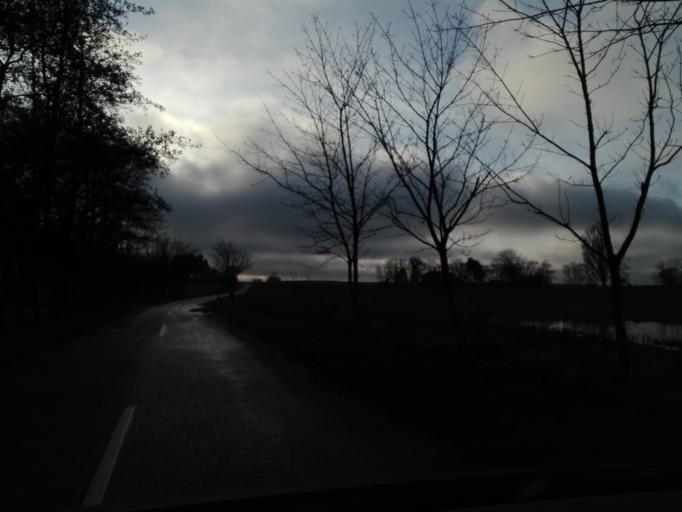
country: DK
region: Central Jutland
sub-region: Arhus Kommune
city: Solbjerg
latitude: 56.0415
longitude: 10.1172
